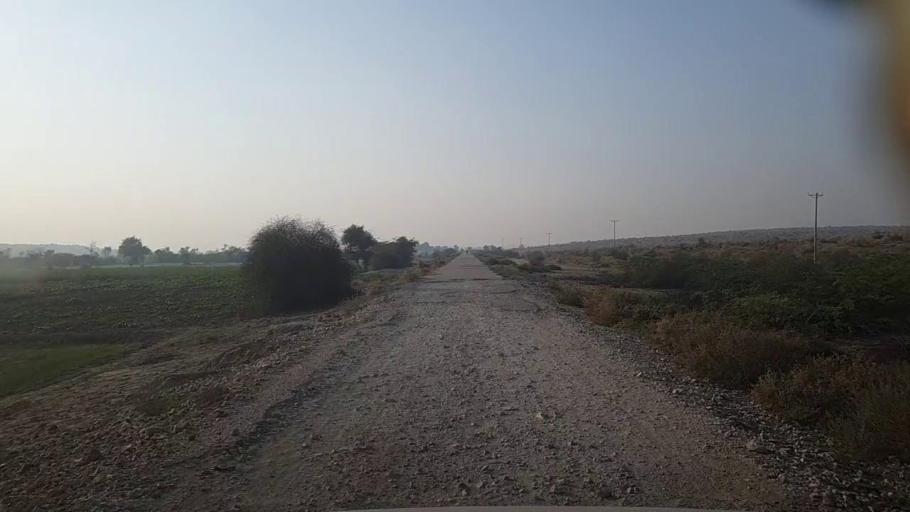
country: PK
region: Sindh
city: Pad Idan
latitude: 26.7138
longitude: 68.4708
